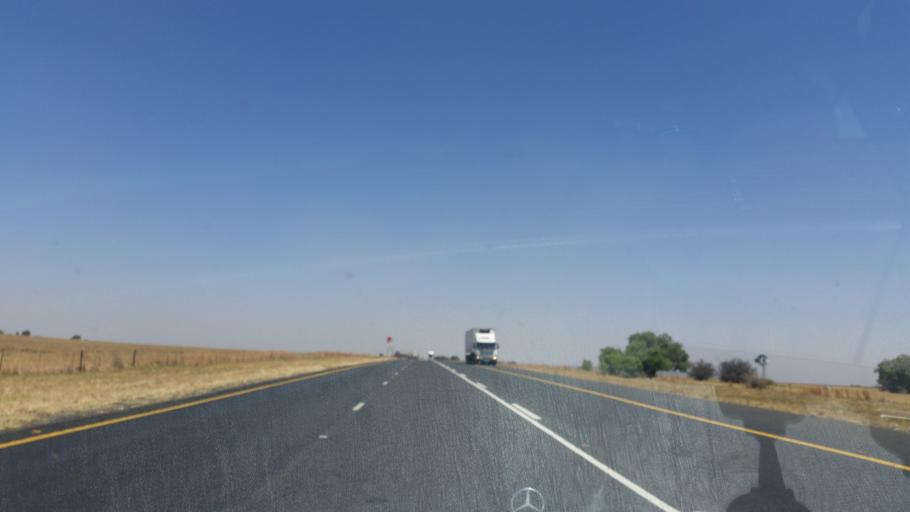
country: ZA
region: Orange Free State
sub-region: Lejweleputswa District Municipality
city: Winburg
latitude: -28.6446
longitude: 26.8844
